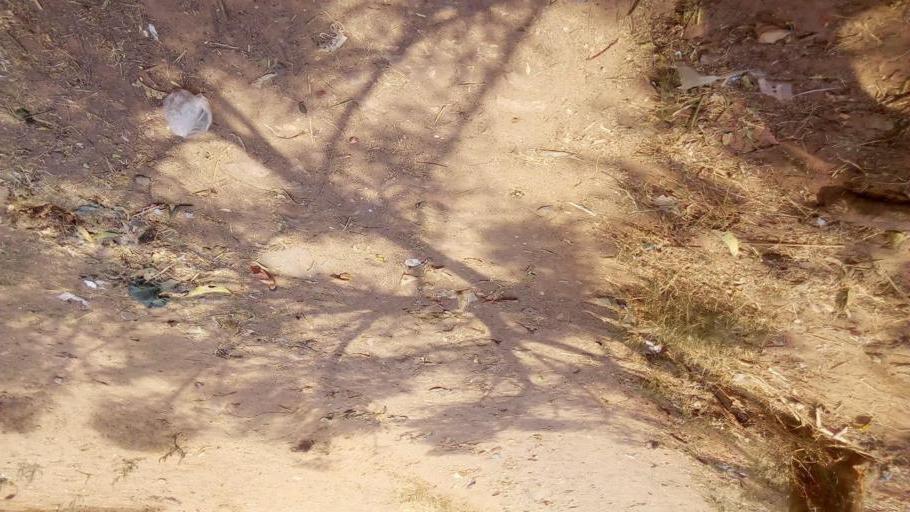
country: ZM
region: Lusaka
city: Lusaka
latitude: -15.3600
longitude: 28.2967
